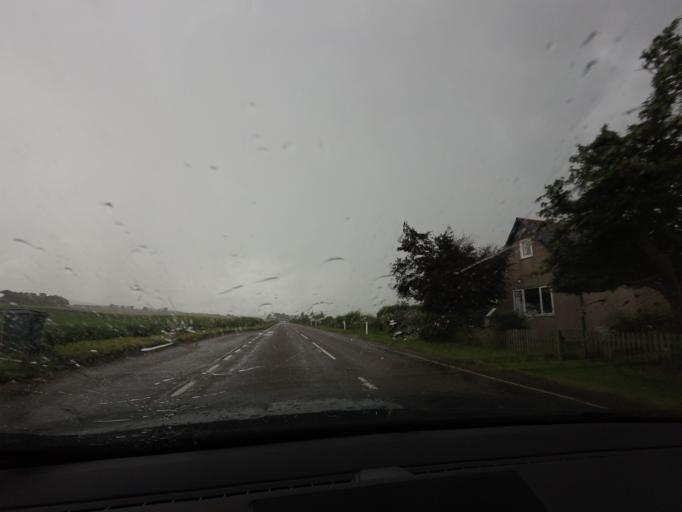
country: GB
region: Scotland
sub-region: Moray
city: Buckie
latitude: 57.6522
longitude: -2.9968
